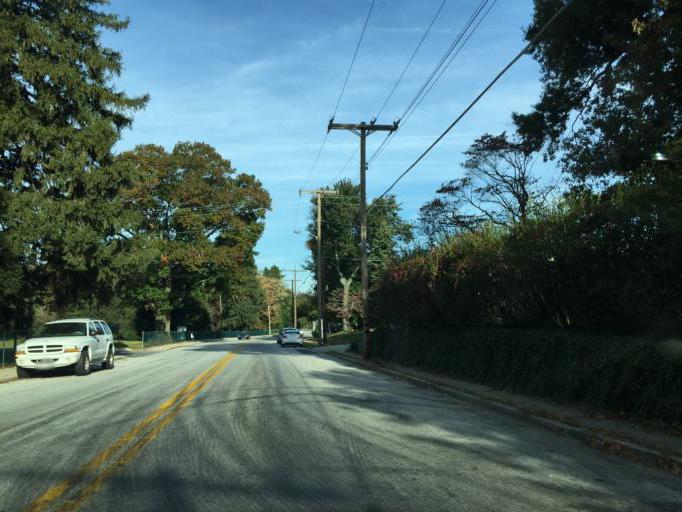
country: US
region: Maryland
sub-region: Baltimore County
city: Towson
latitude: 39.3767
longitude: -76.6202
